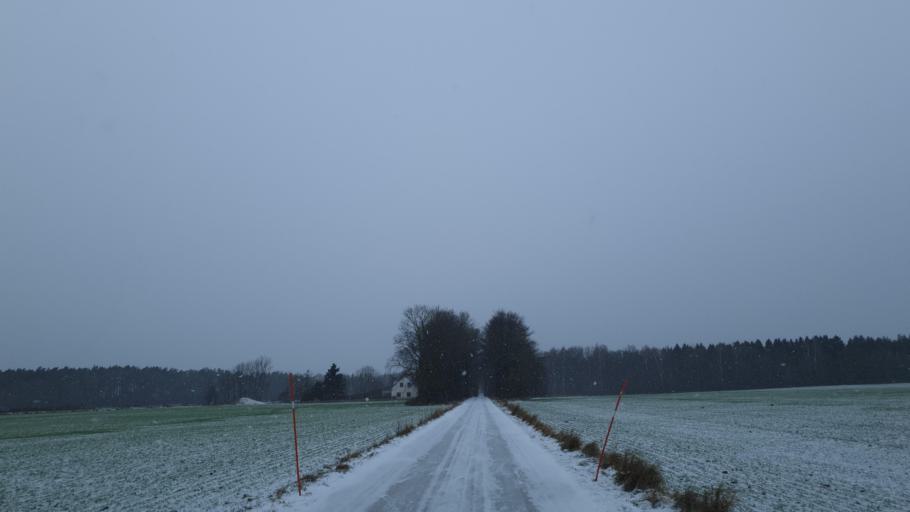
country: SE
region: Gotland
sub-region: Gotland
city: Visby
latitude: 57.5188
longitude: 18.4553
